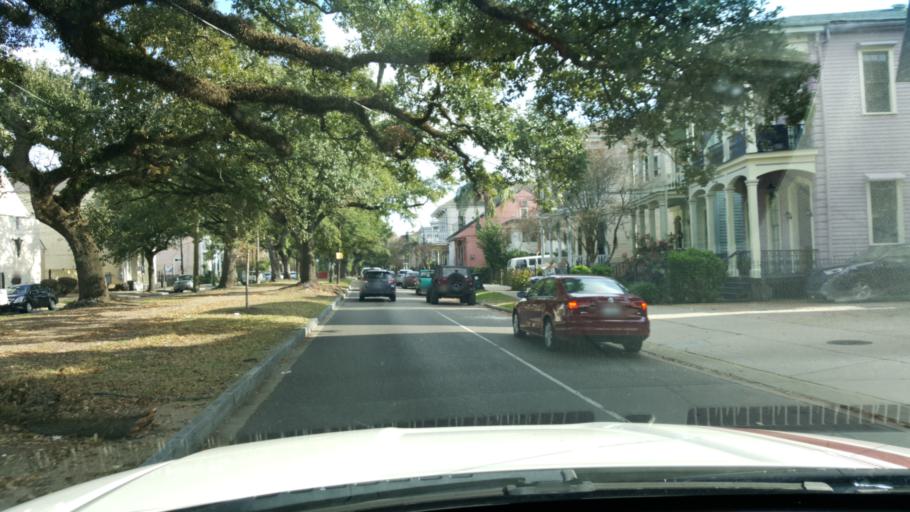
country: US
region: Louisiana
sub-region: Orleans Parish
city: New Orleans
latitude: 29.9681
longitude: -90.0669
